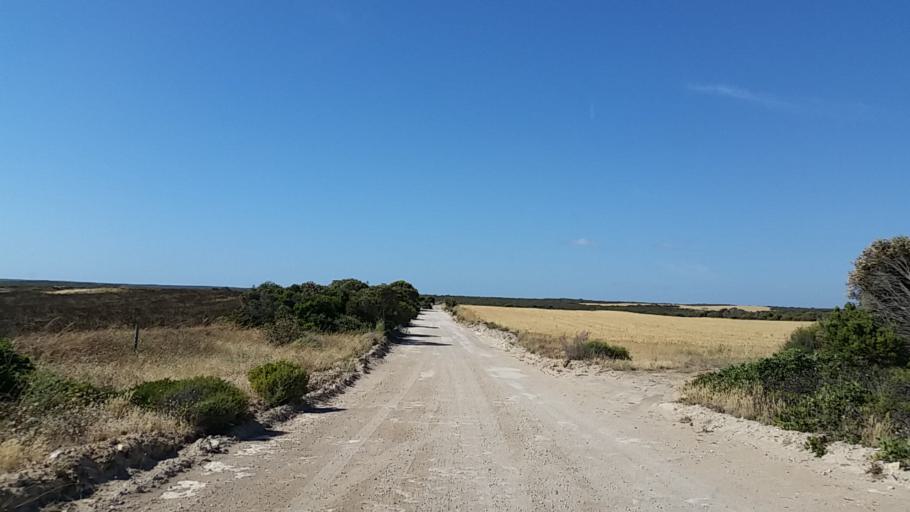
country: AU
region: South Australia
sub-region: Yorke Peninsula
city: Honiton
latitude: -35.2363
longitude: 137.1254
